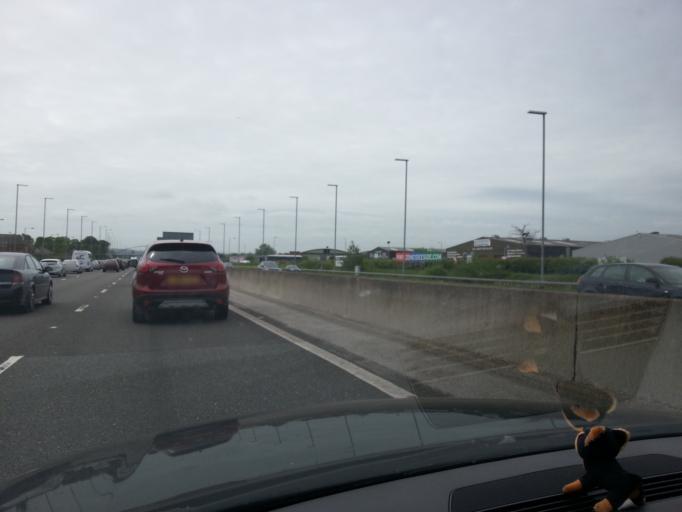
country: GB
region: England
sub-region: Cheshire West and Chester
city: Shotwick
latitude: 53.2275
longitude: -2.9952
